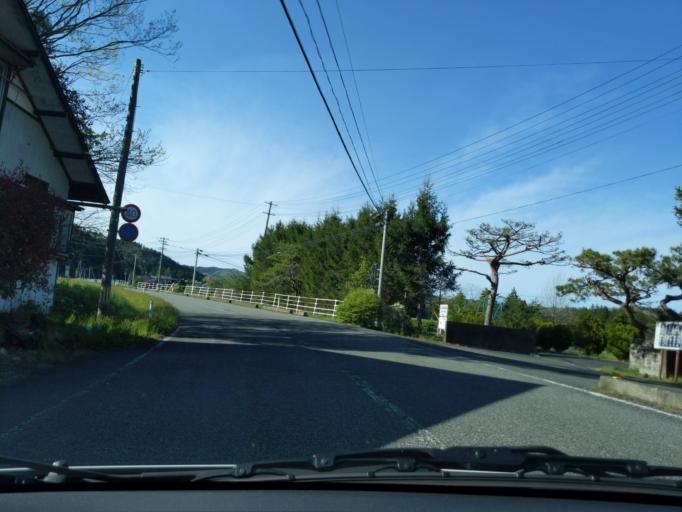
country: JP
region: Iwate
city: Ichinoseki
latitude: 38.8472
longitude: 140.9074
